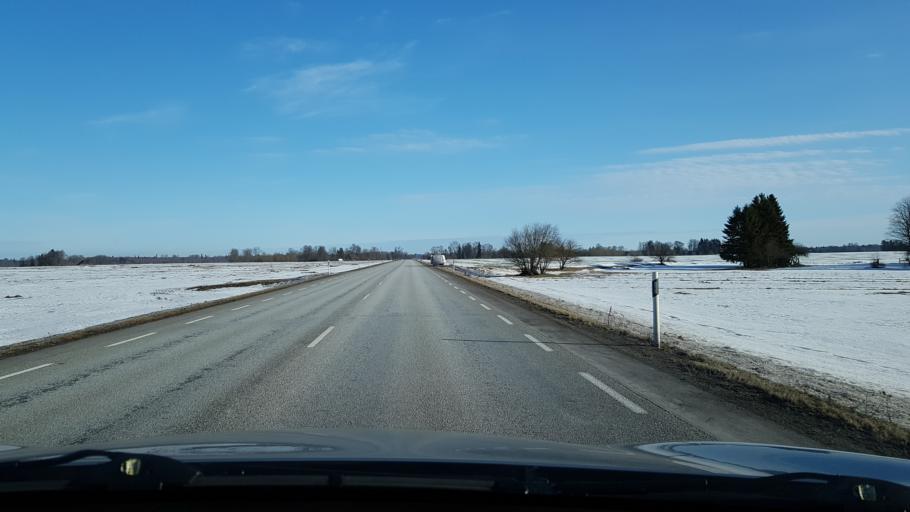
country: EE
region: Viljandimaa
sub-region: Vohma linn
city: Vohma
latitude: 58.6781
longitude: 25.6722
